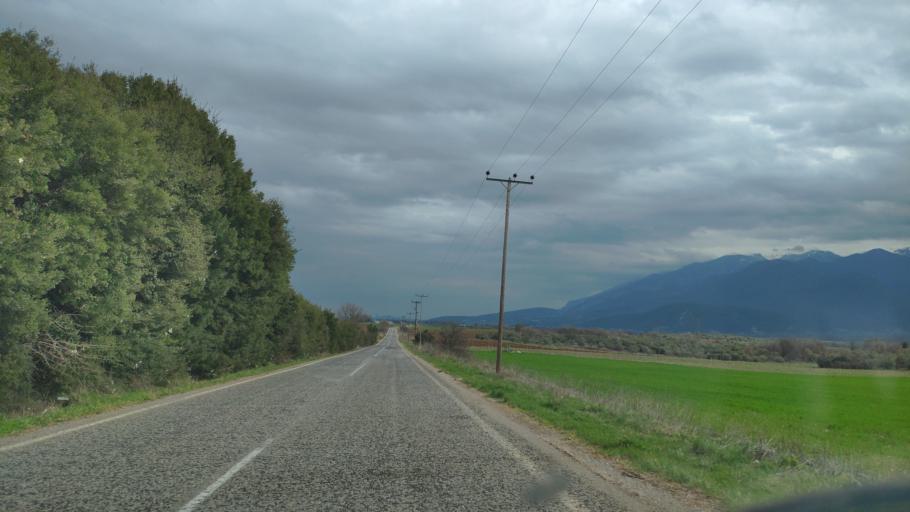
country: GR
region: Central Greece
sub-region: Nomos Fthiotidos
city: Amfikleia
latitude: 38.7024
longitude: 22.5104
